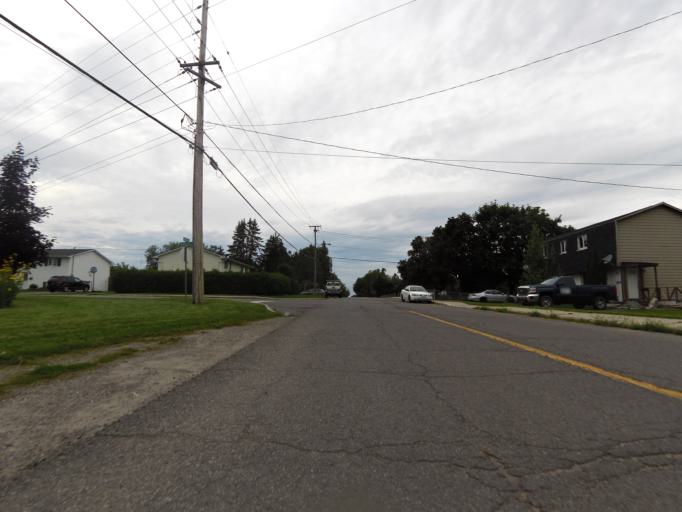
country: CA
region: Ontario
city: Carleton Place
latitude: 45.1443
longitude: -76.1546
